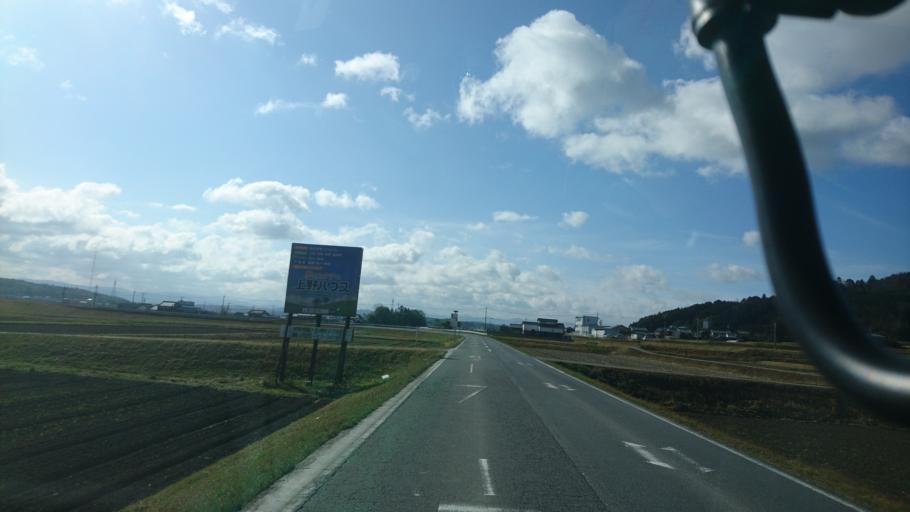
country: JP
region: Mie
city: Ueno-ebisumachi
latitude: 34.7613
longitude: 136.1094
